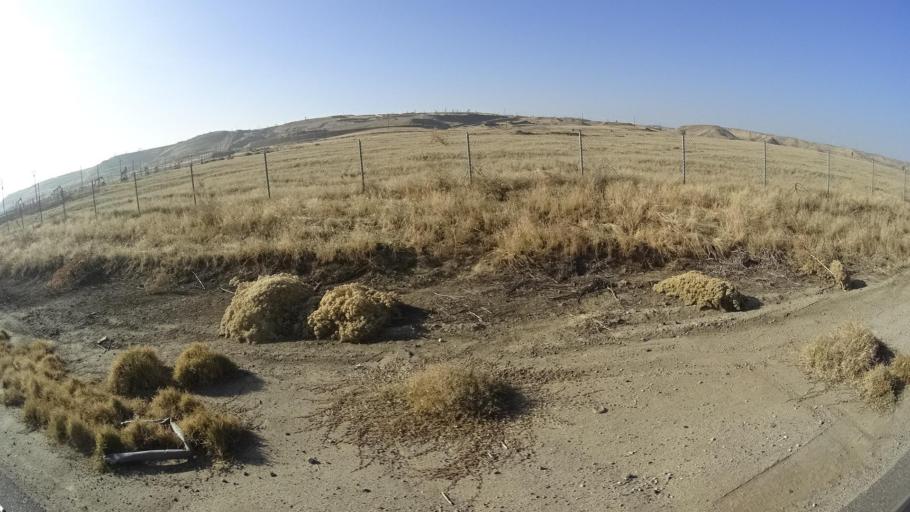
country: US
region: California
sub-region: Kern County
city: Oildale
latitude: 35.4422
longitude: -118.9446
